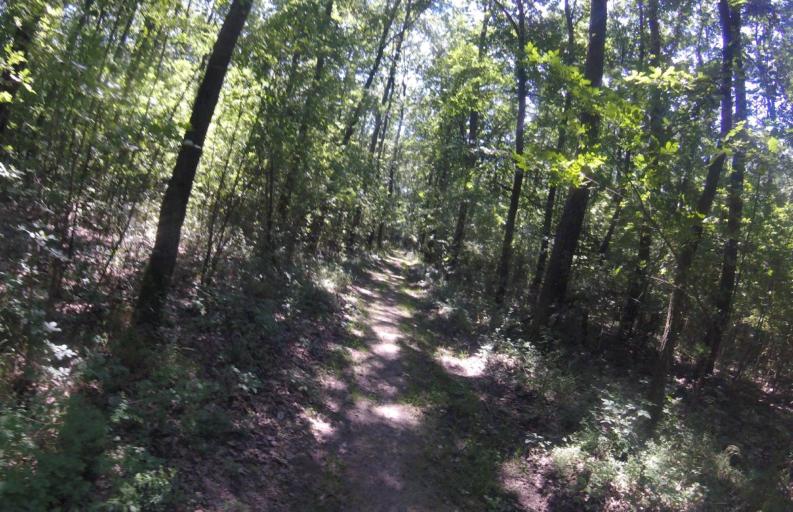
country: HU
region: Pest
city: Szob
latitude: 47.8801
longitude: 18.8721
